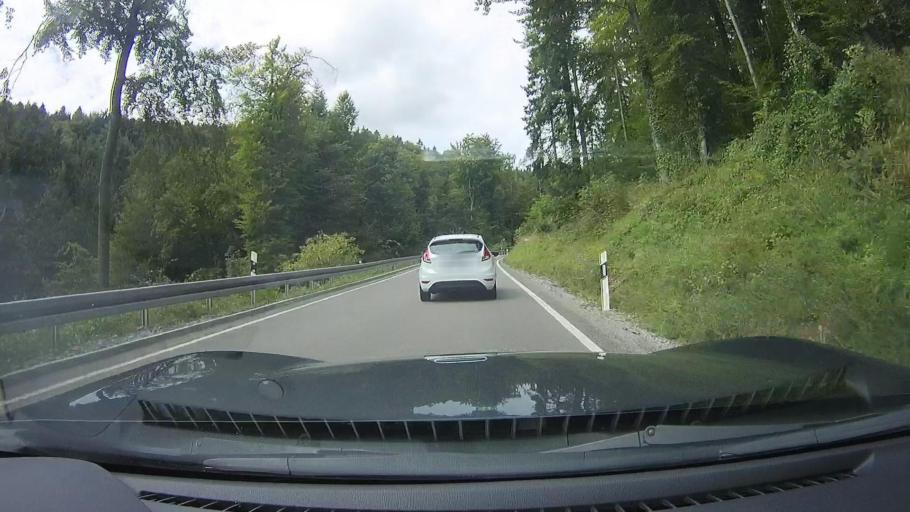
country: DE
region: Baden-Wuerttemberg
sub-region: Regierungsbezirk Stuttgart
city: Althutte
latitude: 48.9041
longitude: 9.5744
